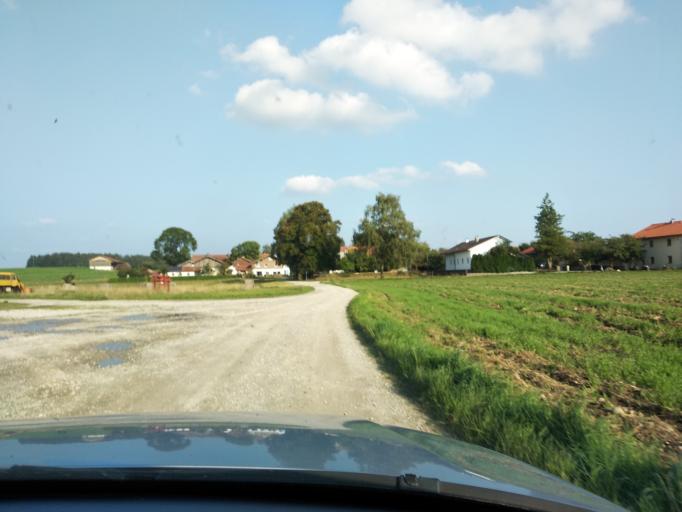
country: DE
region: Bavaria
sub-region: Upper Bavaria
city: Obing
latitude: 47.9943
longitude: 12.4255
